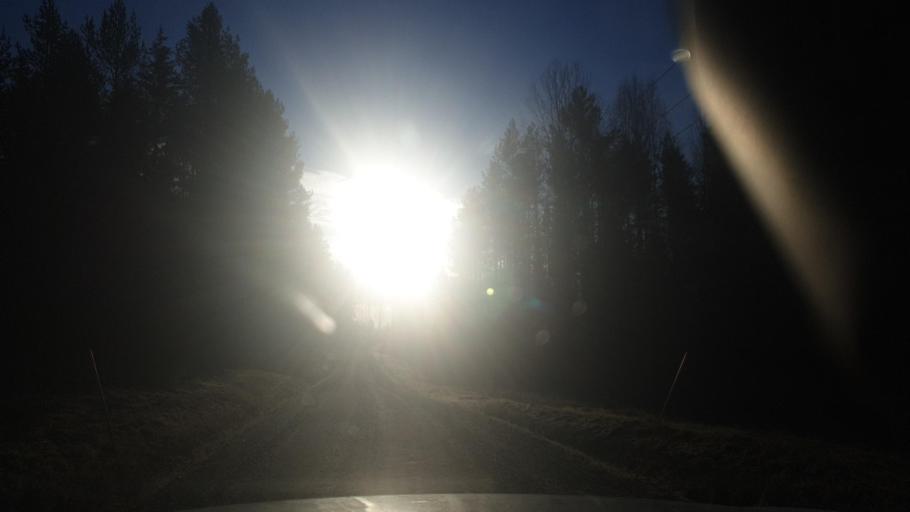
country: SE
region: Vaermland
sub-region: Sunne Kommun
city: Sunne
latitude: 59.6521
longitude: 13.0557
